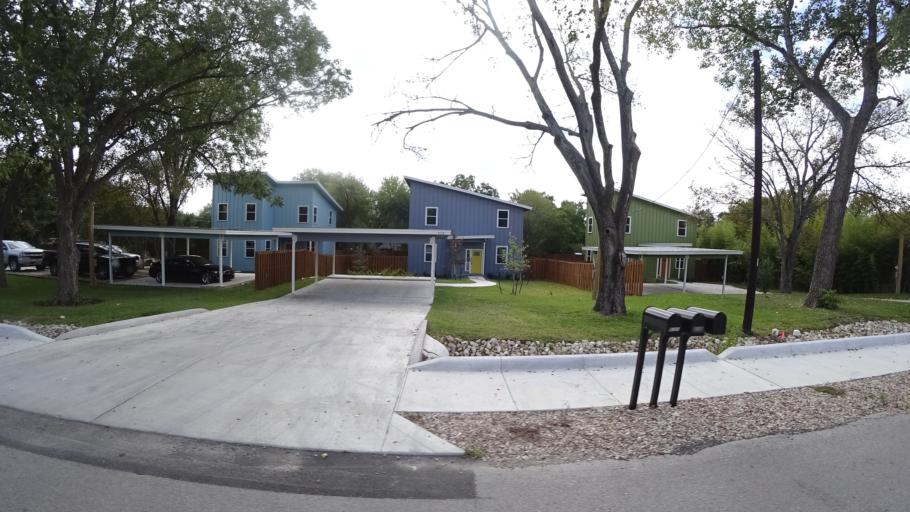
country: US
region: Texas
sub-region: Travis County
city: Austin
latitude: 30.1988
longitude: -97.7357
